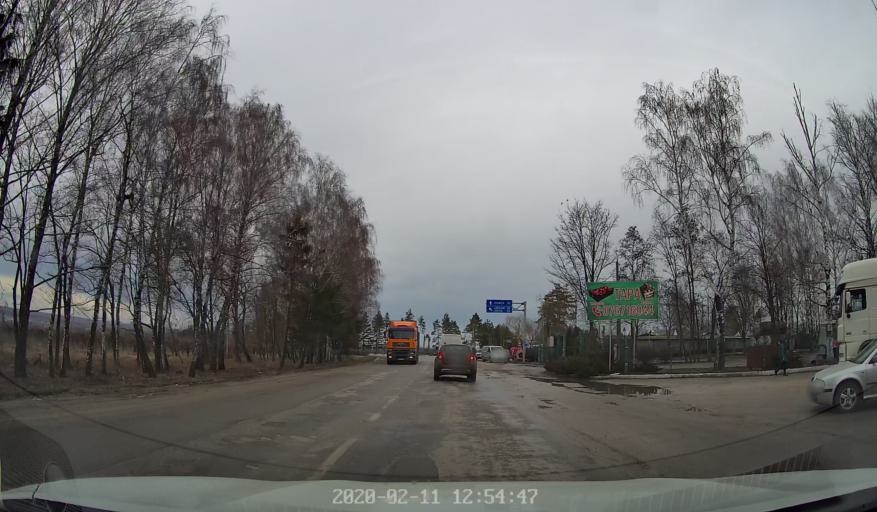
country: MD
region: Briceni
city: Briceni
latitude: 48.3507
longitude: 27.1016
